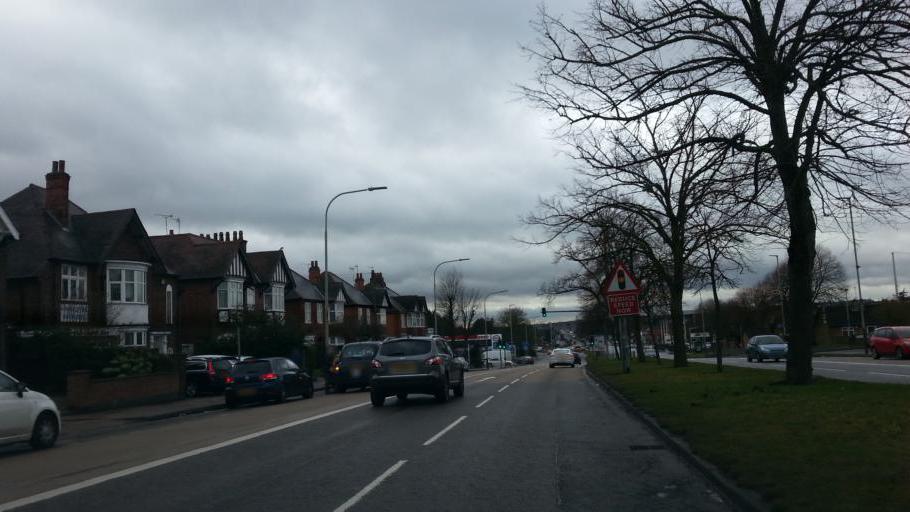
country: GB
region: England
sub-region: Leicestershire
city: Blaby
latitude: 52.6150
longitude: -1.1635
